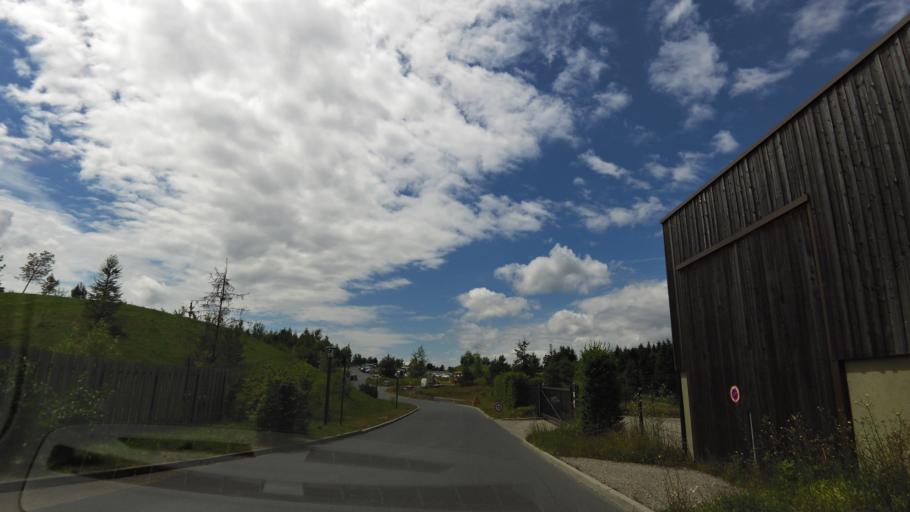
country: FR
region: Lorraine
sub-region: Departement de la Moselle
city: Lorquin
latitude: 48.6215
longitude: 6.9819
